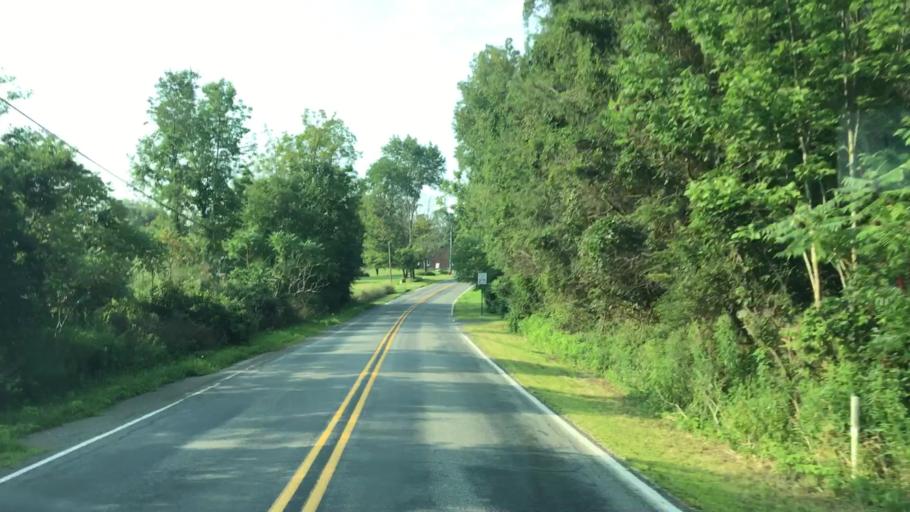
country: US
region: Pennsylvania
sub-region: Lackawanna County
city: Dalton
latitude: 41.6018
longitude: -75.7146
